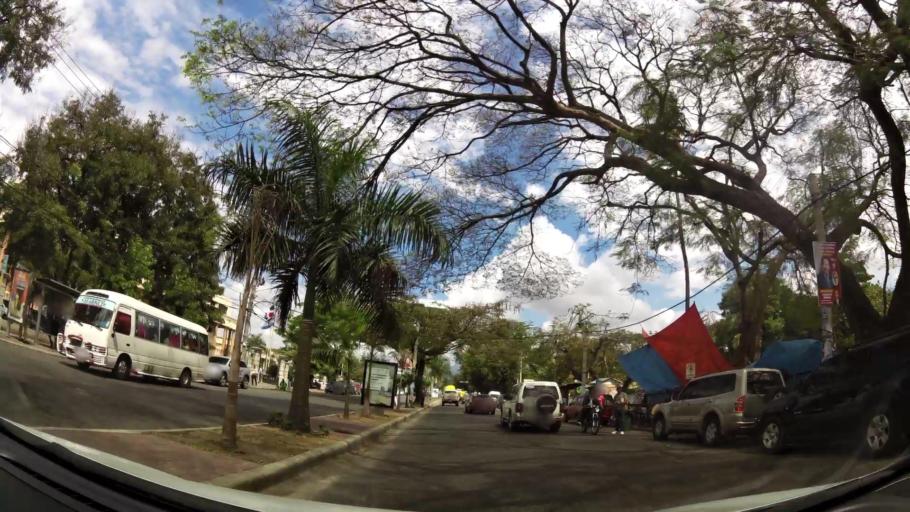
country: DO
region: Santiago
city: Santiago de los Caballeros
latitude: 19.4668
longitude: -70.7119
